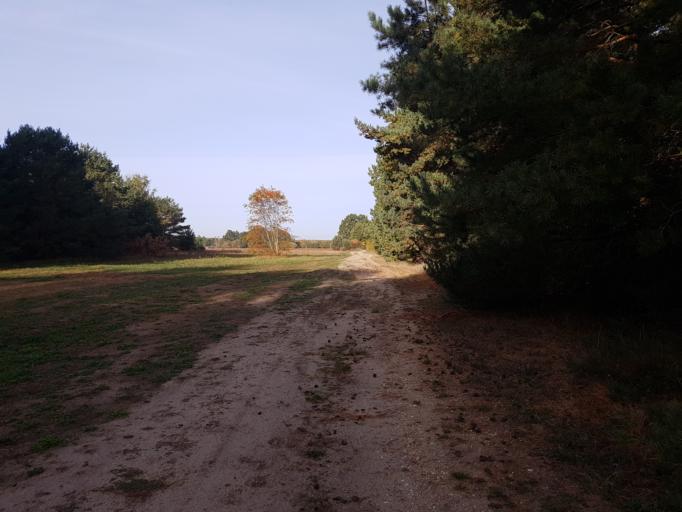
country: DE
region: Brandenburg
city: Niedergorsdorf
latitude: 52.0764
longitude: 12.9692
